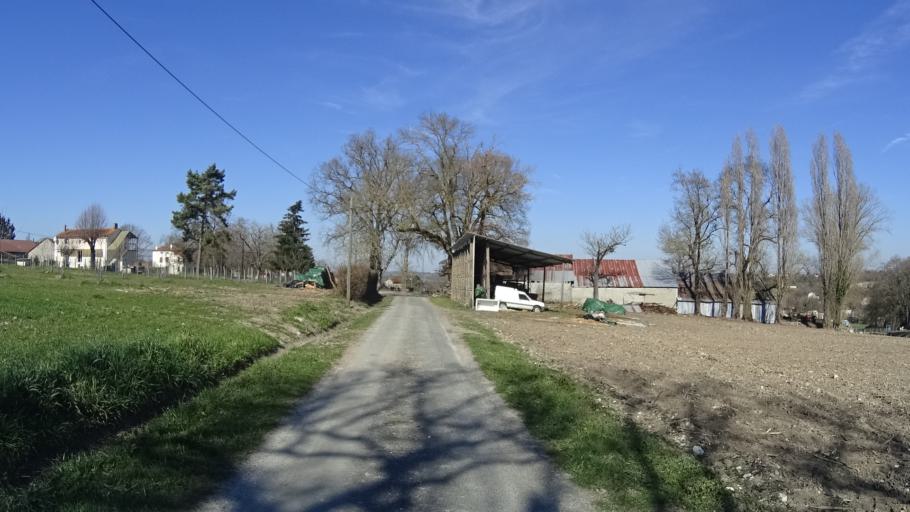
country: FR
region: Aquitaine
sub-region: Departement de la Dordogne
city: Riberac
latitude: 45.2366
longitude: 0.3404
